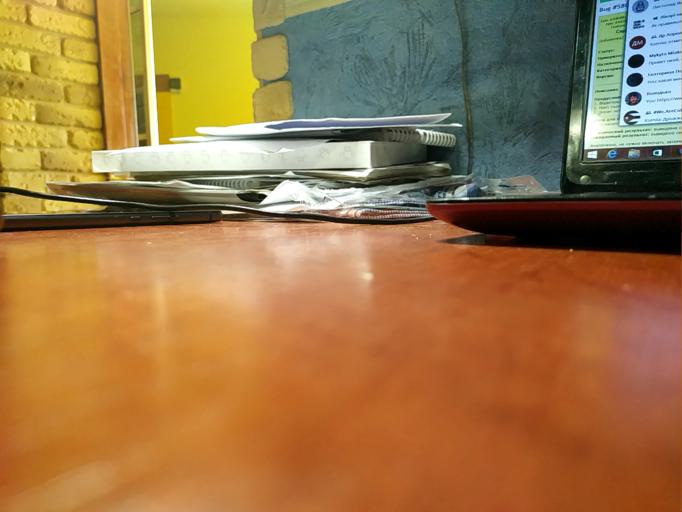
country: RU
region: Vologda
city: Khokhlovo
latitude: 59.4481
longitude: 37.3345
